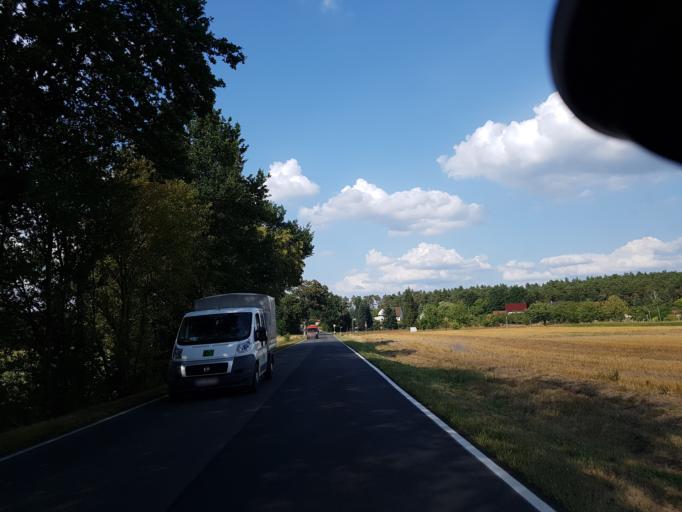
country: DE
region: Brandenburg
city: Calau
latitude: 51.7754
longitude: 13.9539
